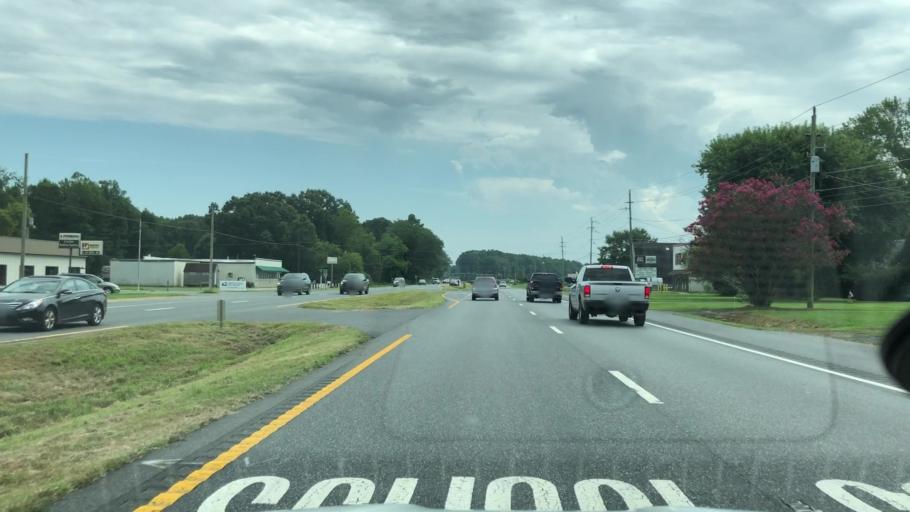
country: US
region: Virginia
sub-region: Accomack County
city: Wattsville
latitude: 37.9279
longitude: -75.5487
